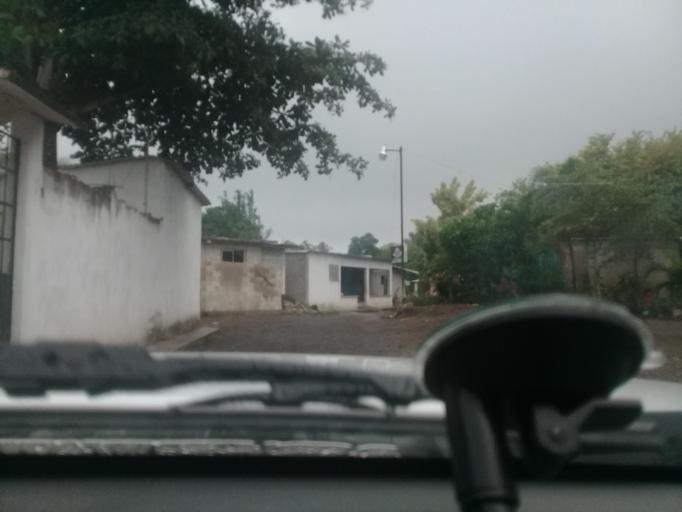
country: MX
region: Veracruz
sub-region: Puente Nacional
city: Chichicaxtle
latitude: 19.3322
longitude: -96.4240
